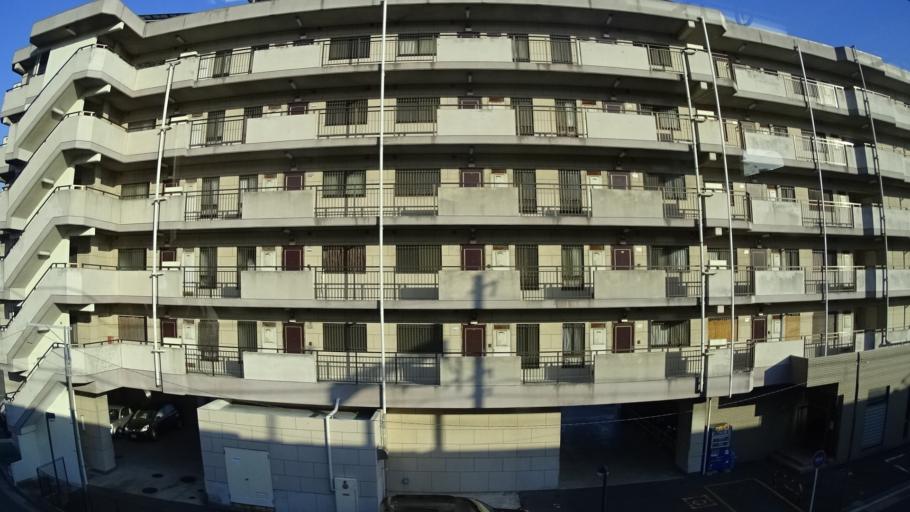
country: JP
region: Kanagawa
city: Yokosuka
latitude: 35.2107
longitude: 139.6840
